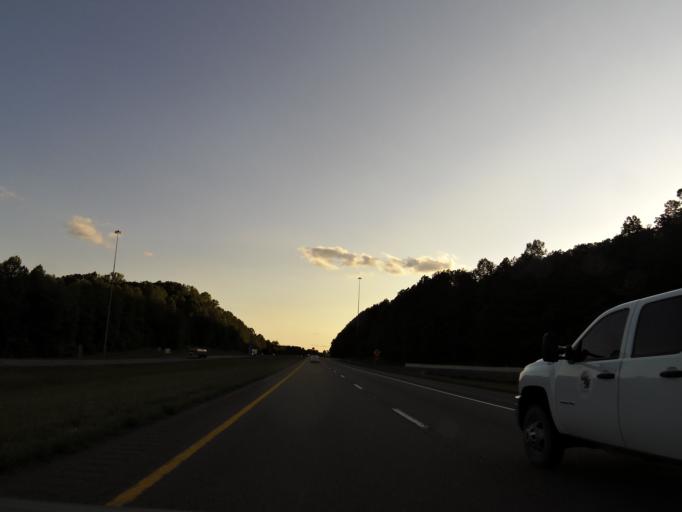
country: US
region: Tennessee
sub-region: Sullivan County
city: Blountville
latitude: 36.5438
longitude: -82.3369
